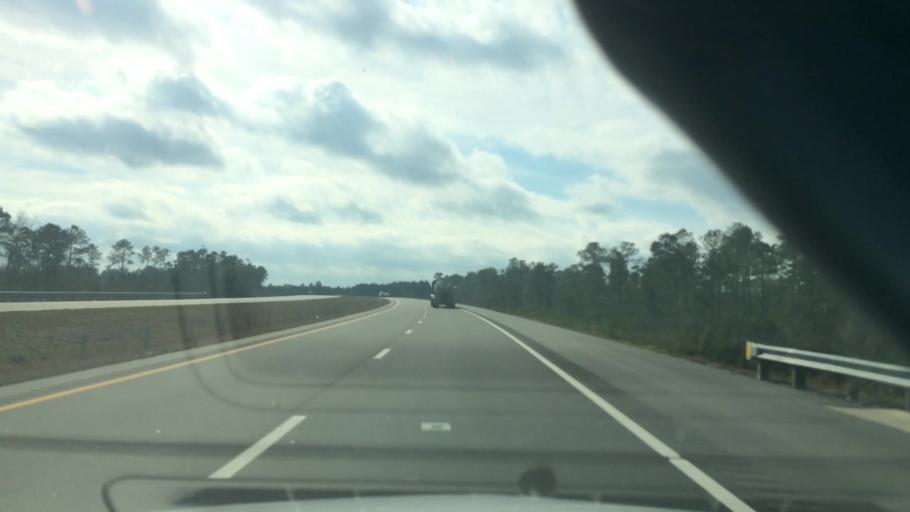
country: US
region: North Carolina
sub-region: Brunswick County
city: Leland
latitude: 34.2754
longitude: -78.0730
